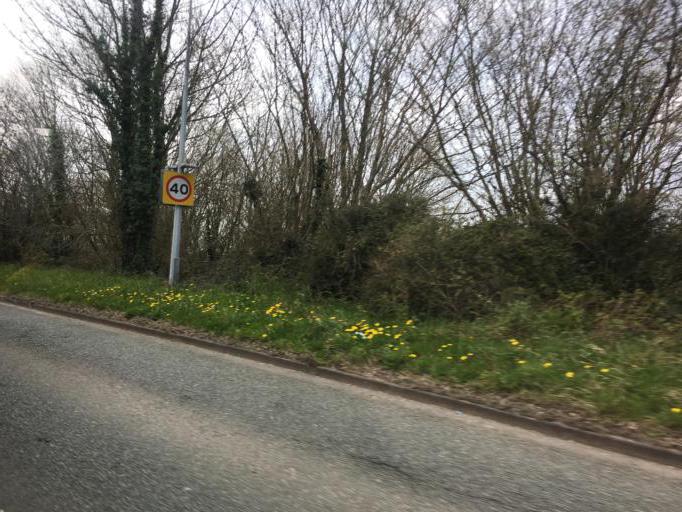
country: GB
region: Wales
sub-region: Gwynedd
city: Y Felinheli
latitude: 53.1772
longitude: -4.2206
